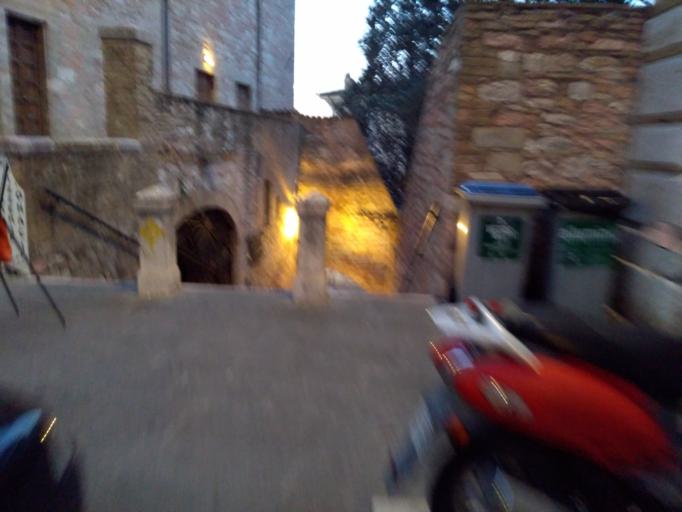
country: IT
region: Umbria
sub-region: Provincia di Perugia
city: Assisi
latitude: 43.0717
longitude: 12.6123
